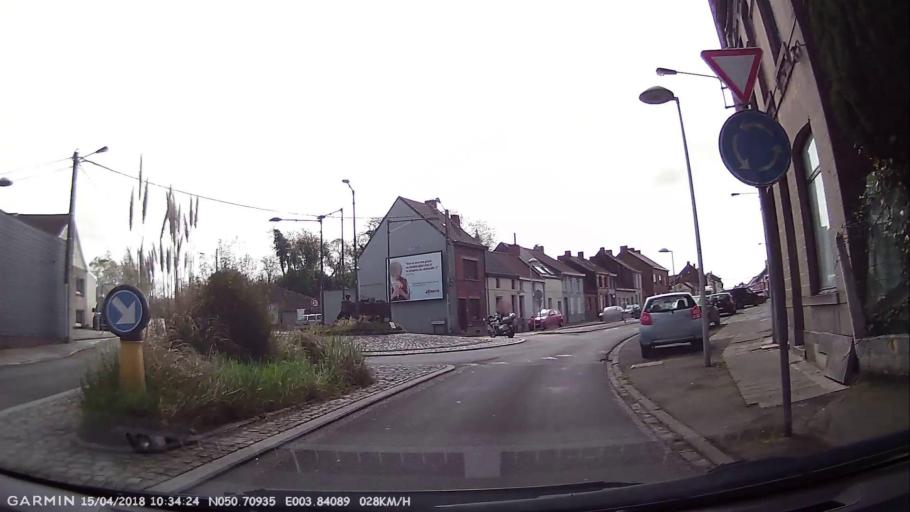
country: BE
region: Wallonia
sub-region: Province du Hainaut
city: Lessines
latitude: 50.7094
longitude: 3.8410
